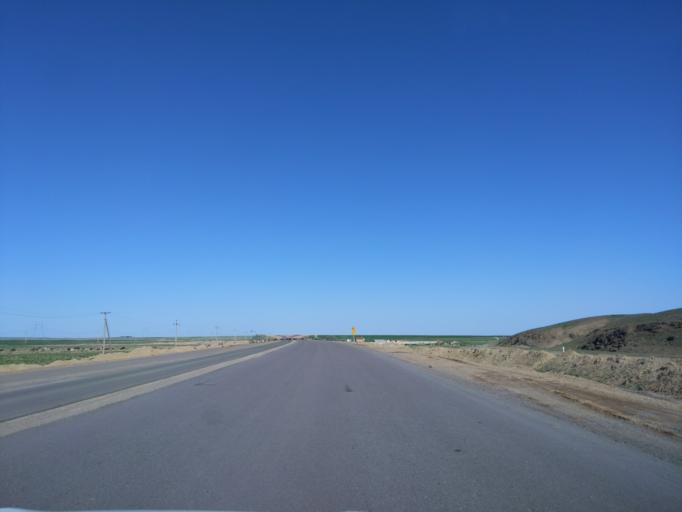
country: KZ
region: Almaty Oblysy
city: Bakanas
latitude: 44.0937
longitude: 75.9878
